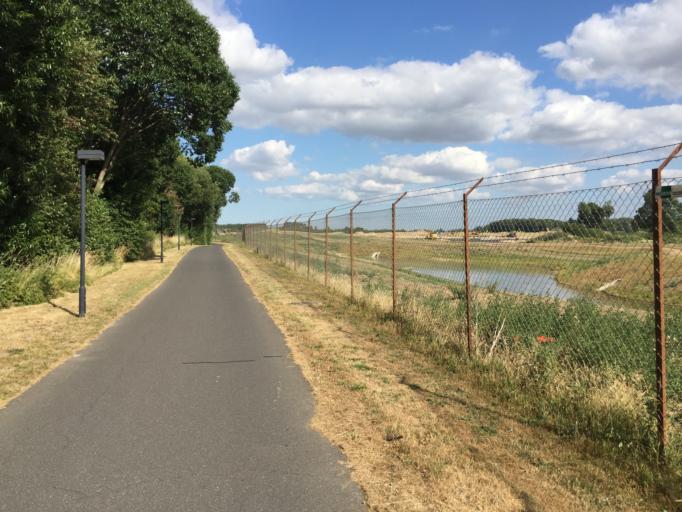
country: DK
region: South Denmark
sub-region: Odense Kommune
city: Hojby
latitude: 55.3631
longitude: 10.4176
